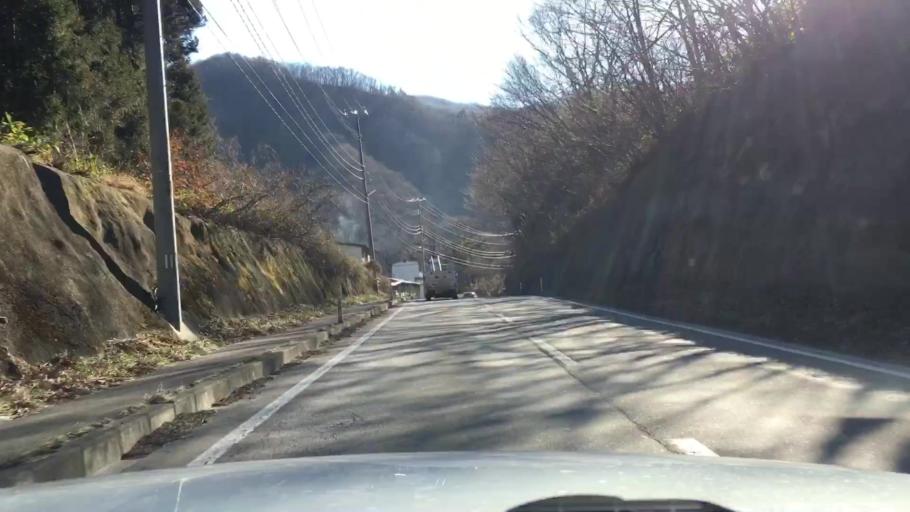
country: JP
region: Iwate
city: Miyako
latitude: 39.6219
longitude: 141.8110
